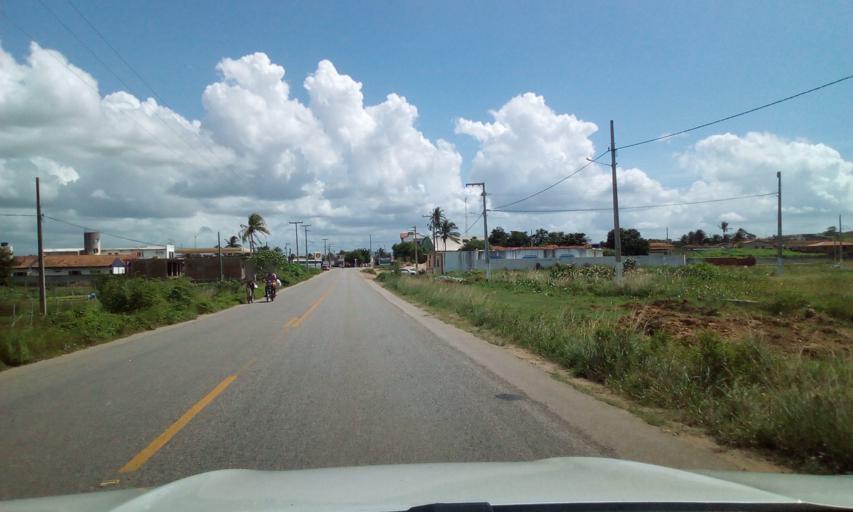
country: BR
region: Paraiba
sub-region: Guarabira
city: Guarabira
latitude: -6.8500
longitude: -35.3726
